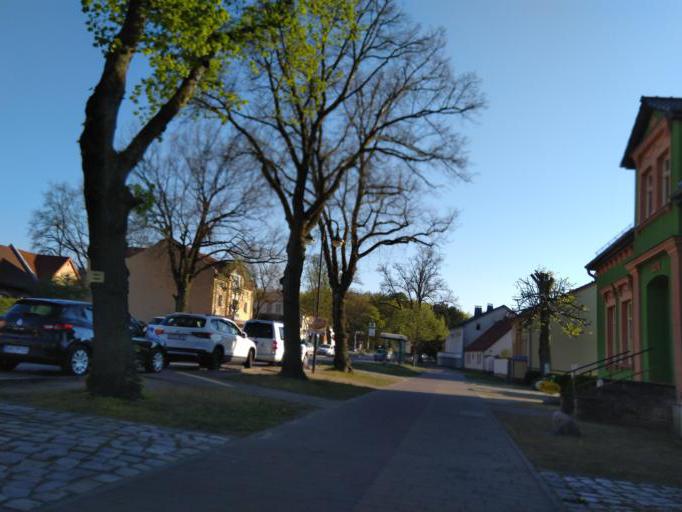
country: DE
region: Berlin
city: Buch
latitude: 52.6523
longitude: 13.5414
